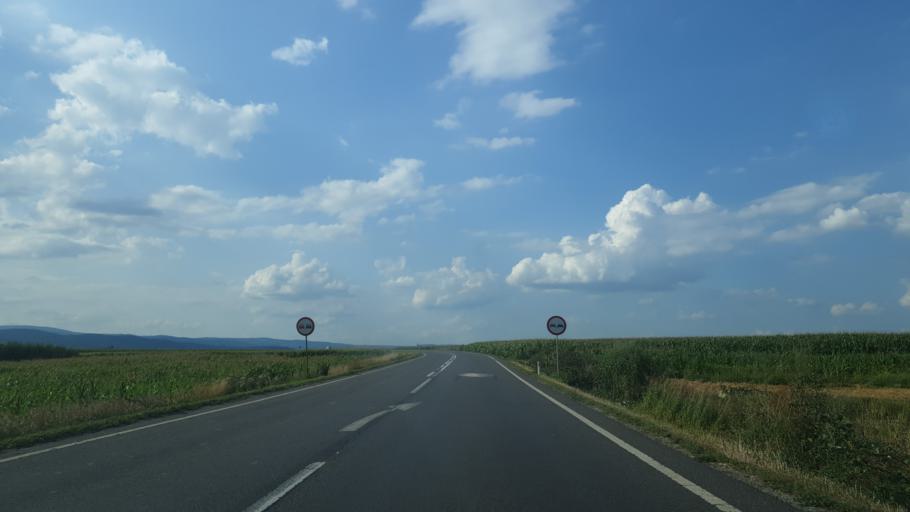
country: RO
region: Covasna
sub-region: Comuna Chichis
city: Chichis
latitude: 45.7903
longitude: 25.8067
